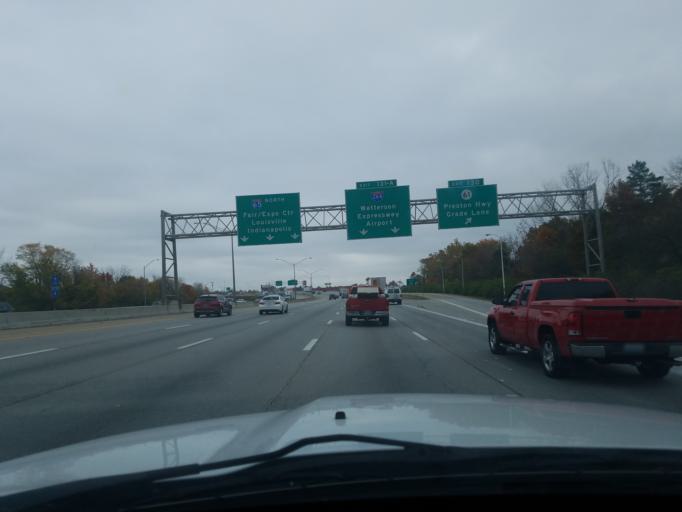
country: US
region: Kentucky
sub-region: Jefferson County
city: Audubon Park
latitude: 38.1735
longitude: -85.7199
